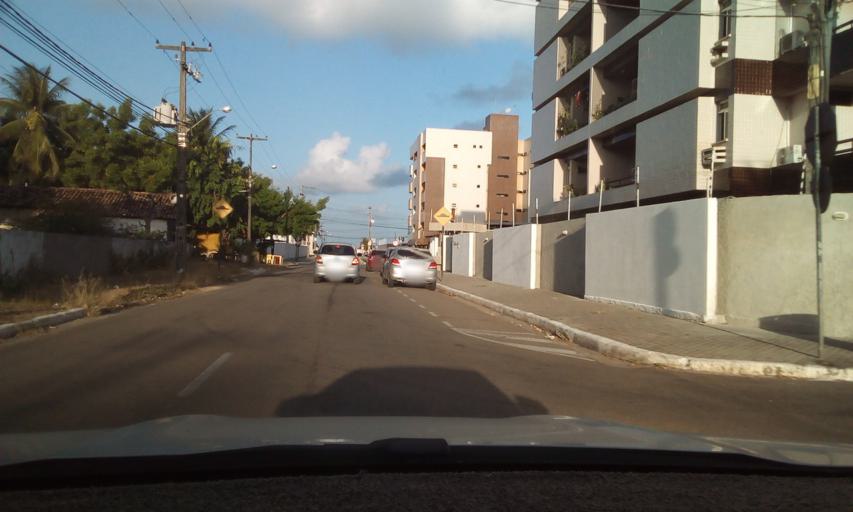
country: BR
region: Paraiba
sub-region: Joao Pessoa
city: Joao Pessoa
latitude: -7.0738
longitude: -34.8330
